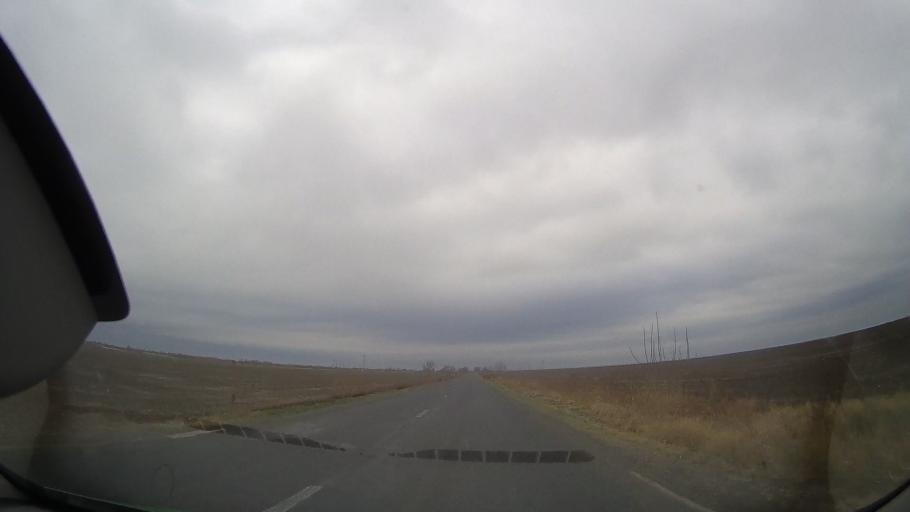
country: RO
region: Buzau
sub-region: Comuna Padina
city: Padina
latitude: 44.7887
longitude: 27.1454
